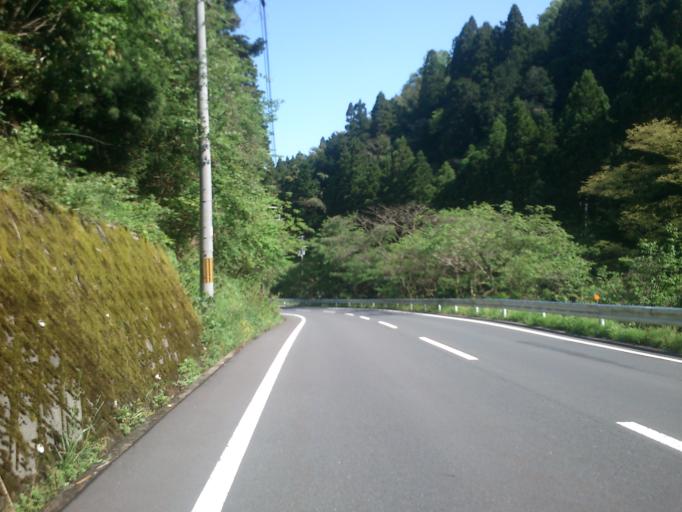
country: JP
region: Kyoto
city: Miyazu
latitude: 35.6447
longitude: 135.1294
